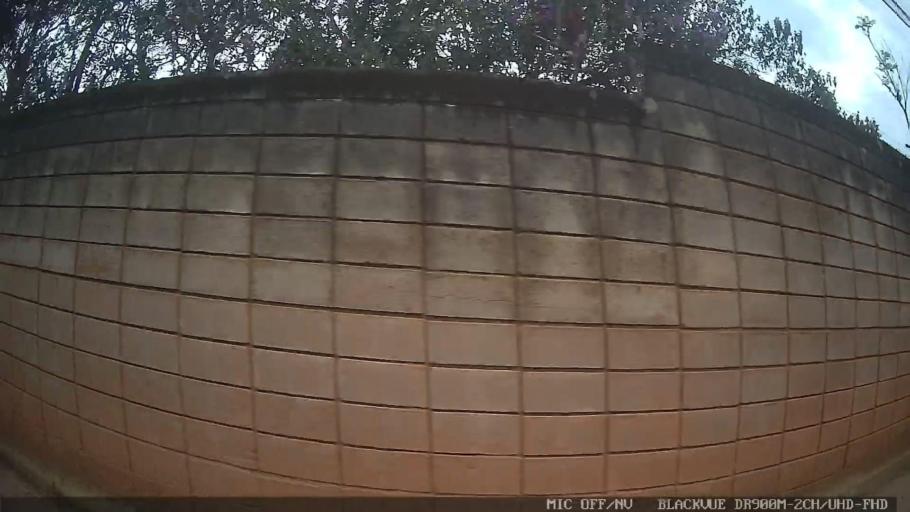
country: BR
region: Sao Paulo
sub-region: Atibaia
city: Atibaia
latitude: -23.1537
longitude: -46.5912
